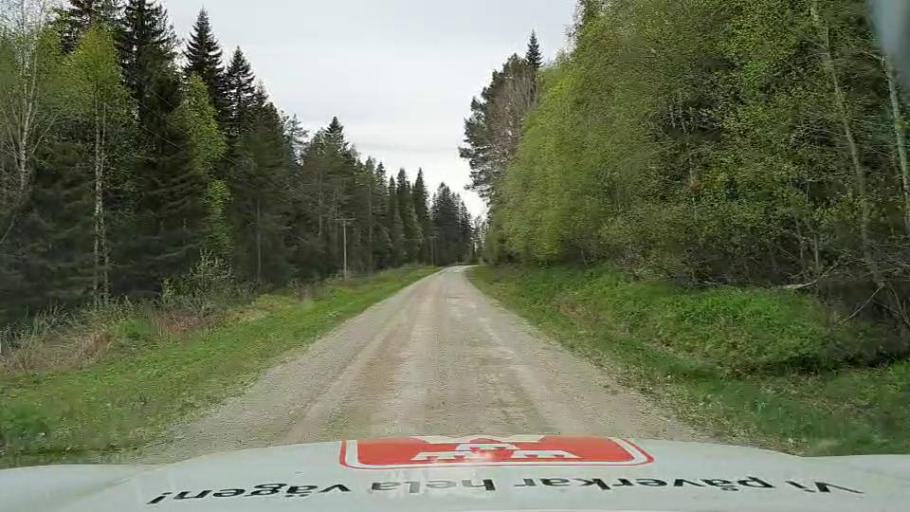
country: SE
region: Jaemtland
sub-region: Bergs Kommun
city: Hoverberg
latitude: 62.6696
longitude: 14.8103
